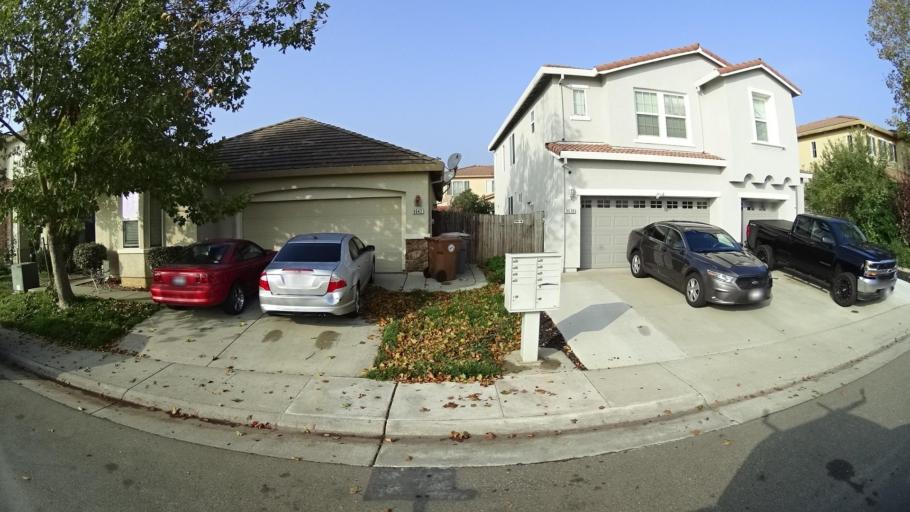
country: US
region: California
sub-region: Sacramento County
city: Elk Grove
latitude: 38.4066
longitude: -121.3509
